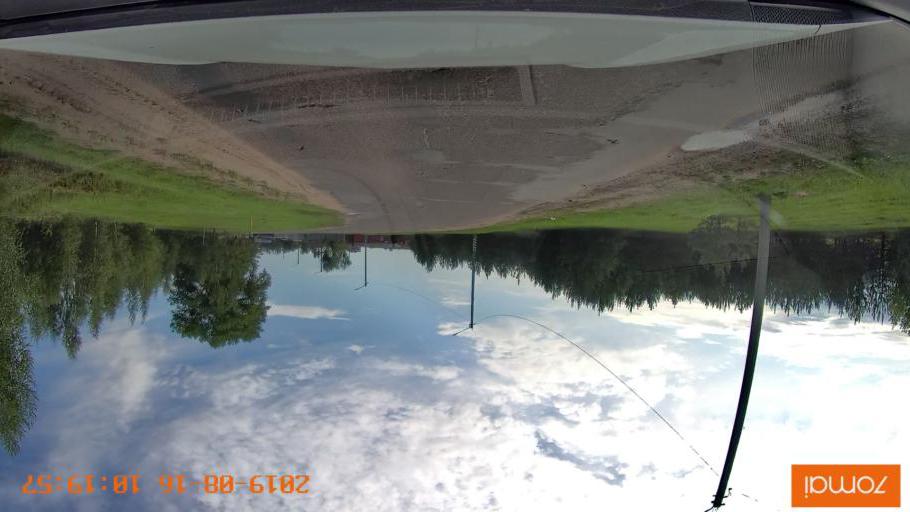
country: BY
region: Mogilev
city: Asipovichy
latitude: 53.3046
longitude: 28.6641
